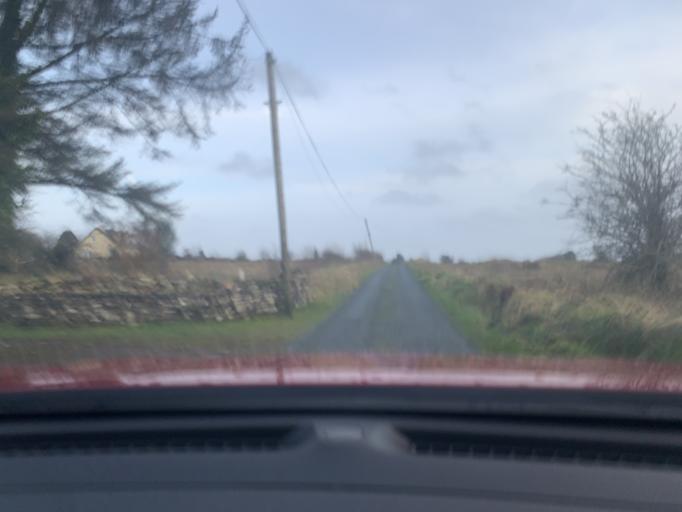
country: IE
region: Connaught
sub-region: Roscommon
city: Ballaghaderreen
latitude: 53.9568
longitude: -8.5332
